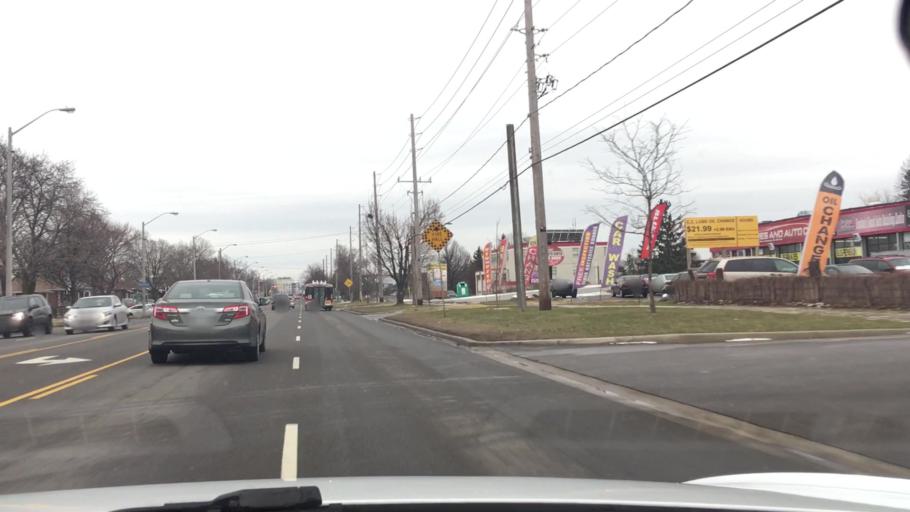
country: CA
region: Ontario
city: Scarborough
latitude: 43.7660
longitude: -79.2278
